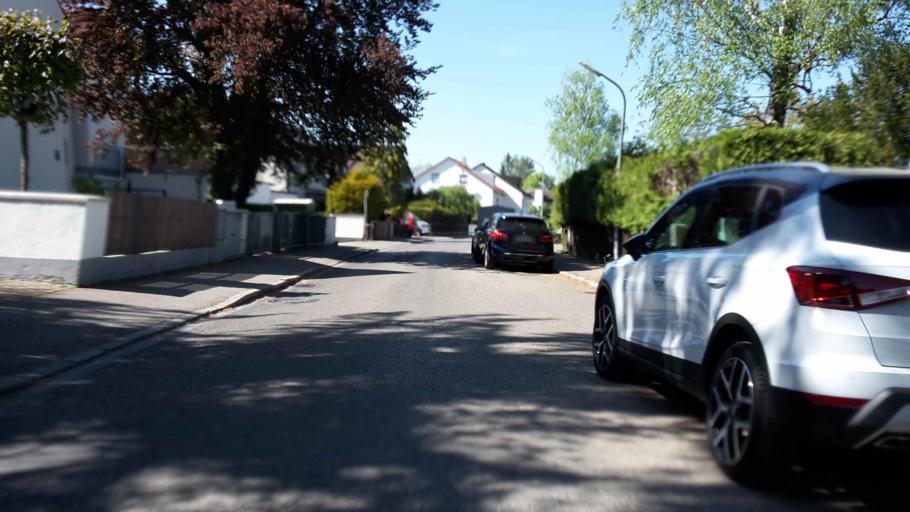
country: DE
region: Bavaria
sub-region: Upper Bavaria
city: Karlsfeld
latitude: 48.1838
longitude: 11.4466
